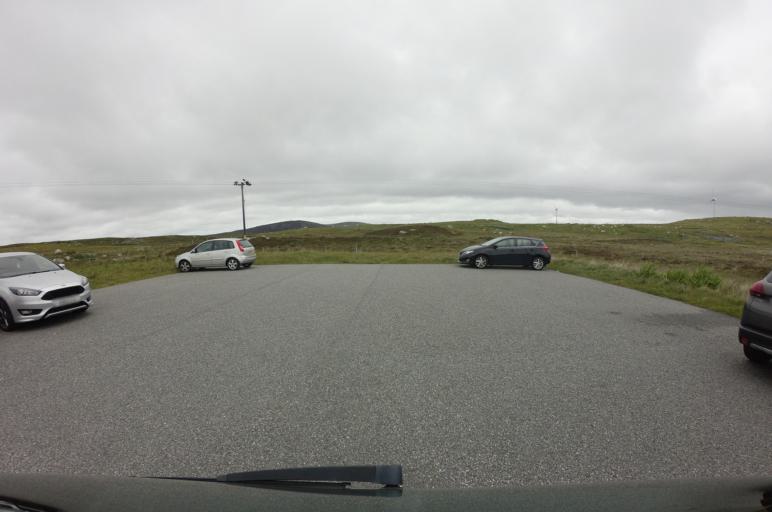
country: GB
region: Scotland
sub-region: Eilean Siar
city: Isle of North Uist
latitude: 57.5552
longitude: -7.3399
